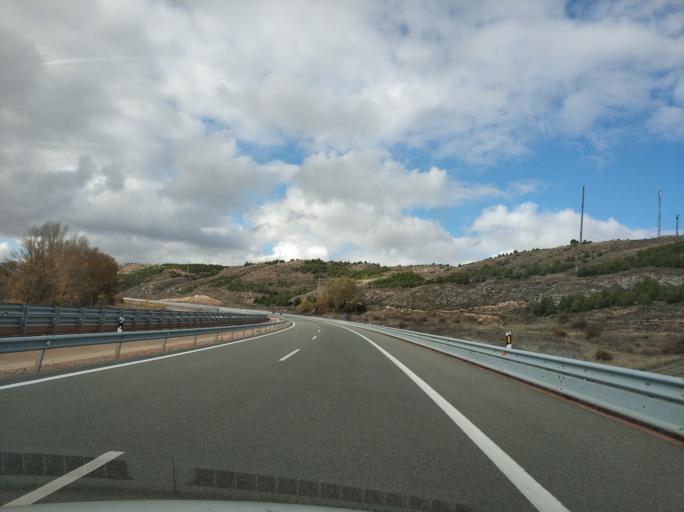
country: ES
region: Castille and Leon
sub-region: Provincia de Soria
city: Medinaceli
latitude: 41.1916
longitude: -2.4330
